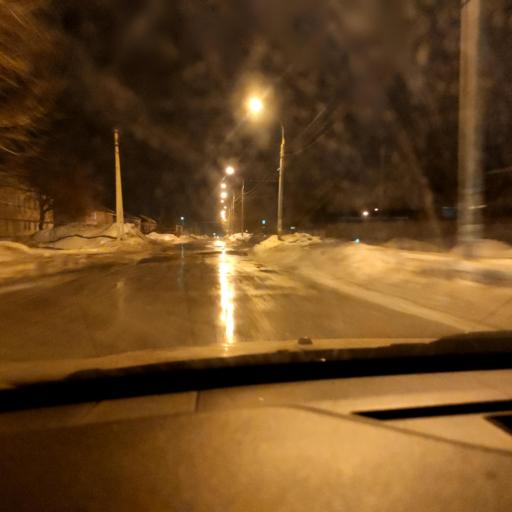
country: RU
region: Samara
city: Smyshlyayevka
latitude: 53.2587
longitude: 50.3891
